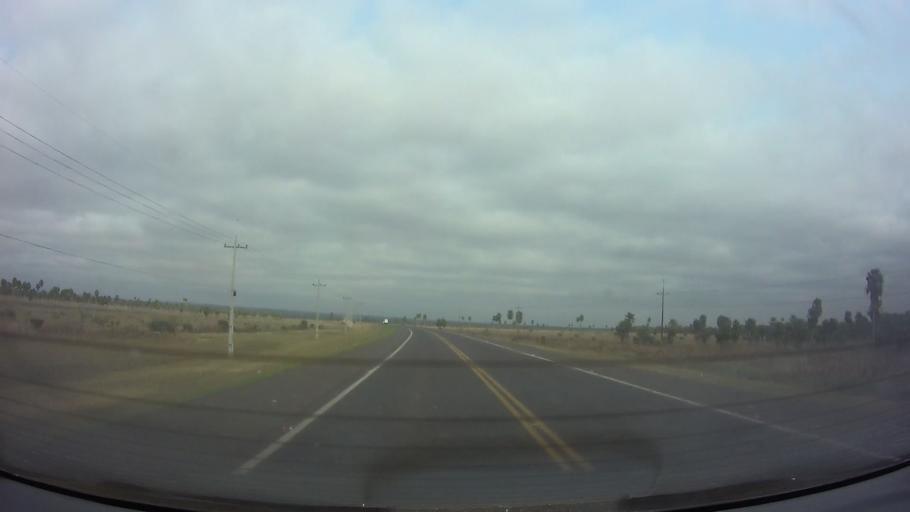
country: PY
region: Cordillera
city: Emboscada
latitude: -25.0713
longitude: -57.2550
